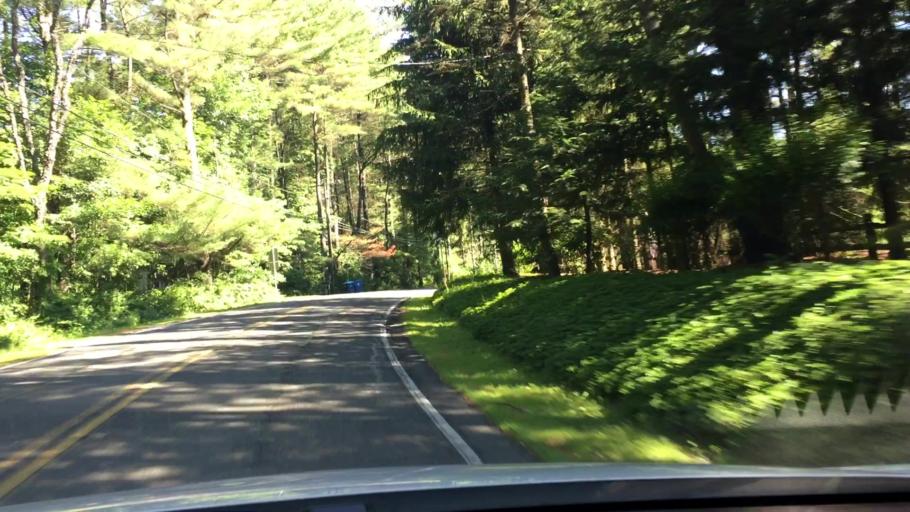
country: US
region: Massachusetts
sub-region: Berkshire County
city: West Stockbridge
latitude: 42.3133
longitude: -73.3702
